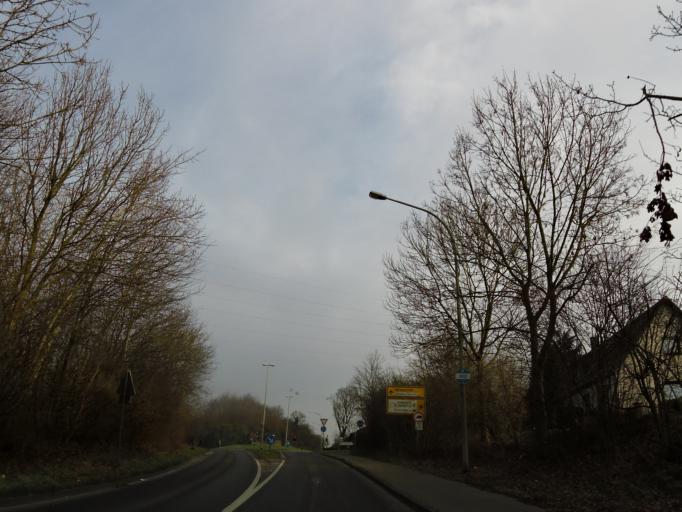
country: DE
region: North Rhine-Westphalia
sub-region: Regierungsbezirk Koln
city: Herzogenrath
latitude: 50.8457
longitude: 6.1011
